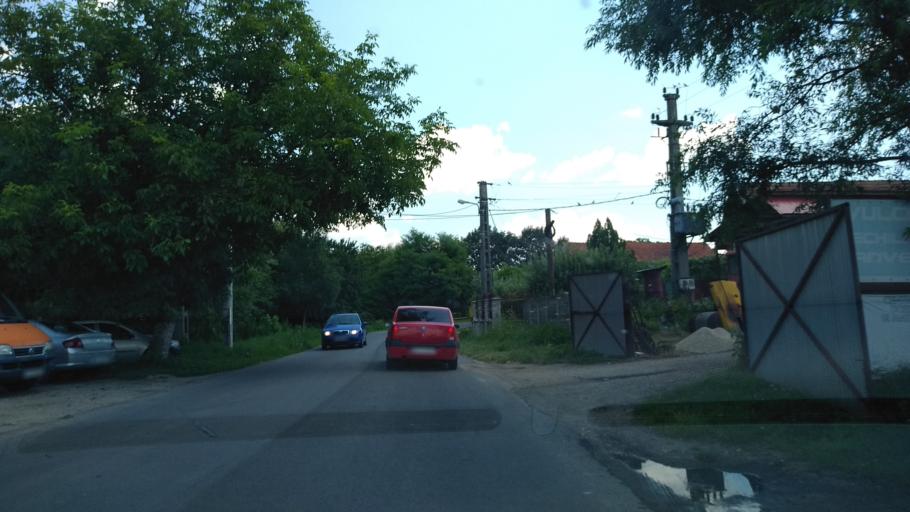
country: RO
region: Hunedoara
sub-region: Comuna Calan
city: Calan
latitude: 45.7204
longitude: 23.0305
